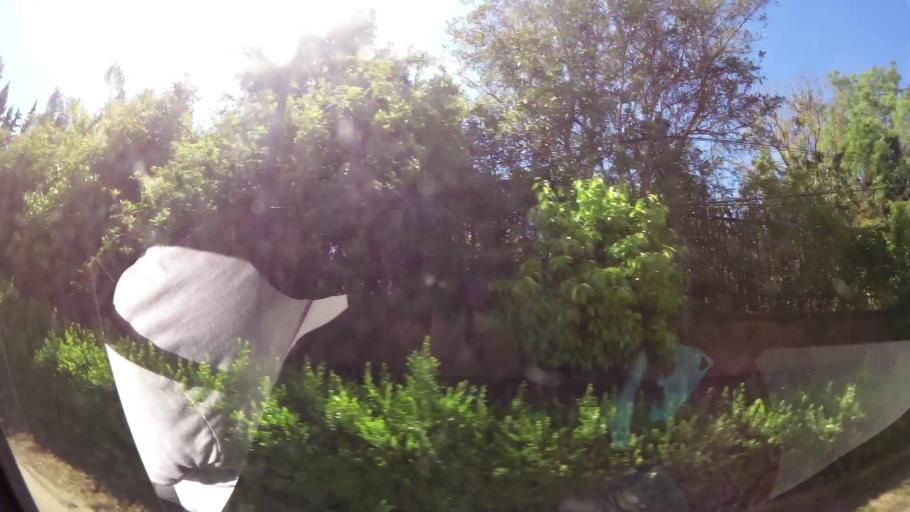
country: MA
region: Marrakech-Tensift-Al Haouz
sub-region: Marrakech
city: Marrakesh
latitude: 31.6555
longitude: -7.9654
